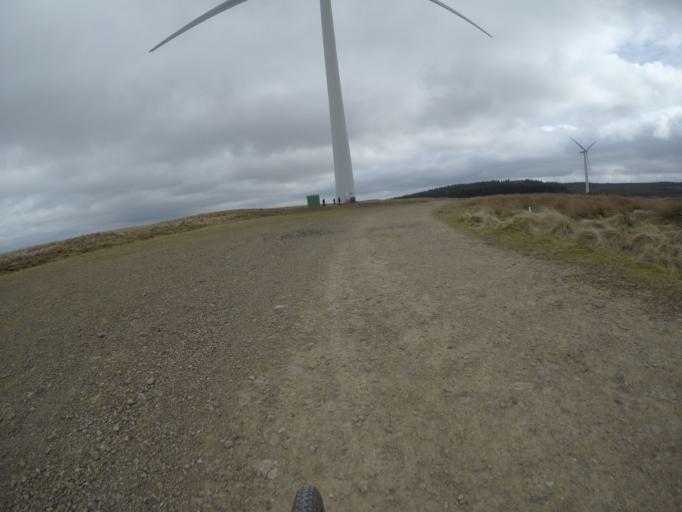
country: GB
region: Scotland
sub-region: East Renfrewshire
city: Eaglesham
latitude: 55.7080
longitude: -4.3024
